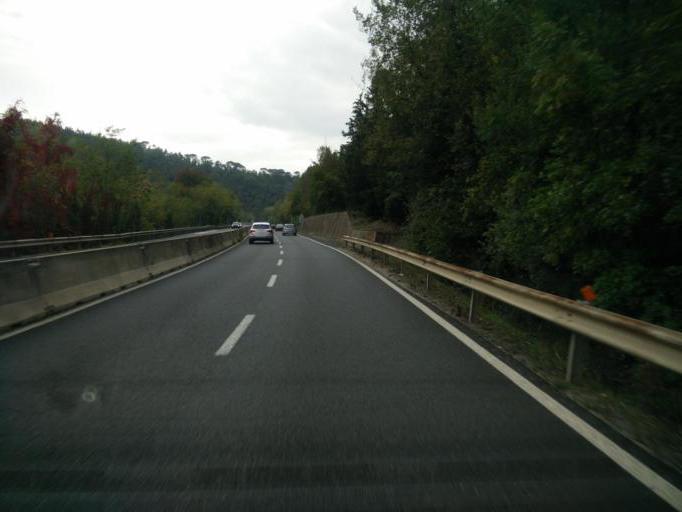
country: IT
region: Tuscany
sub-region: Province of Florence
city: Tavarnuzze
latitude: 43.6928
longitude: 11.2130
